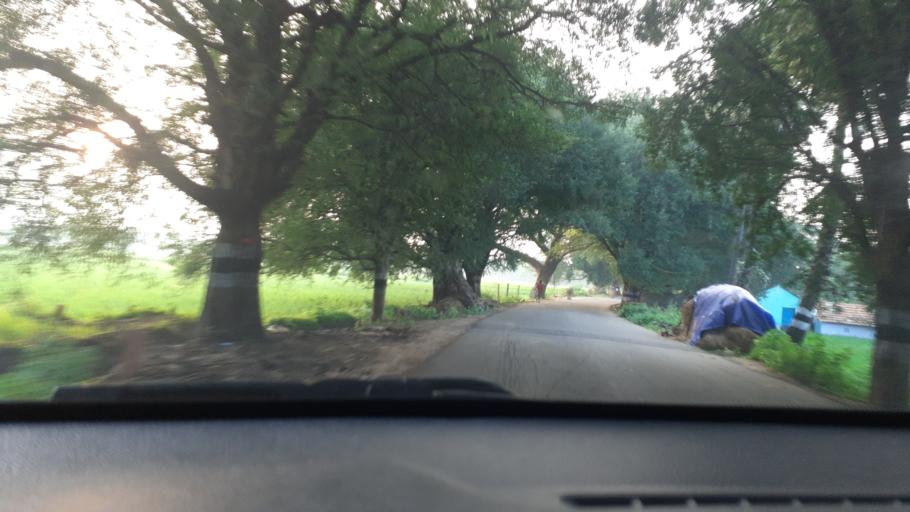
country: IN
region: Tamil Nadu
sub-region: Dindigul
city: Ayakudi
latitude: 10.4085
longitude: 77.5411
